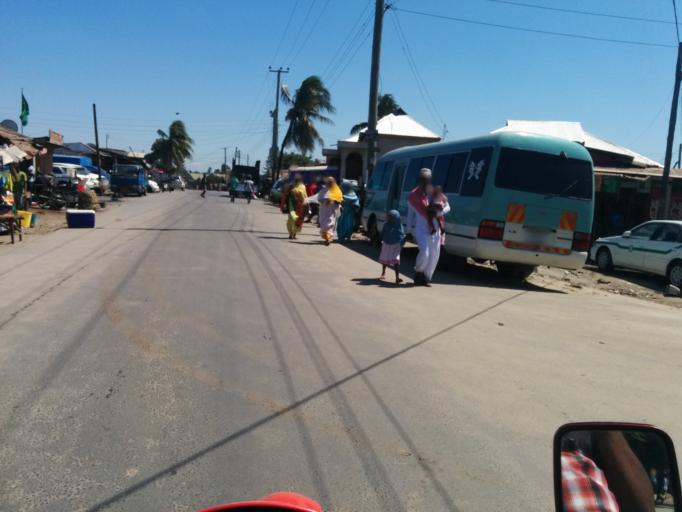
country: TZ
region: Dar es Salaam
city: Magomeni
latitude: -6.7966
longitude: 39.2467
